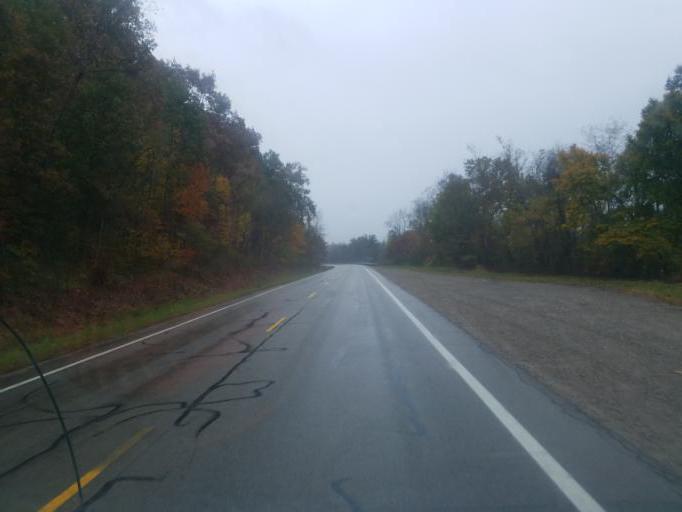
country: US
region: Ohio
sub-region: Muskingum County
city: North Zanesville
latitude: 40.0096
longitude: -82.0848
